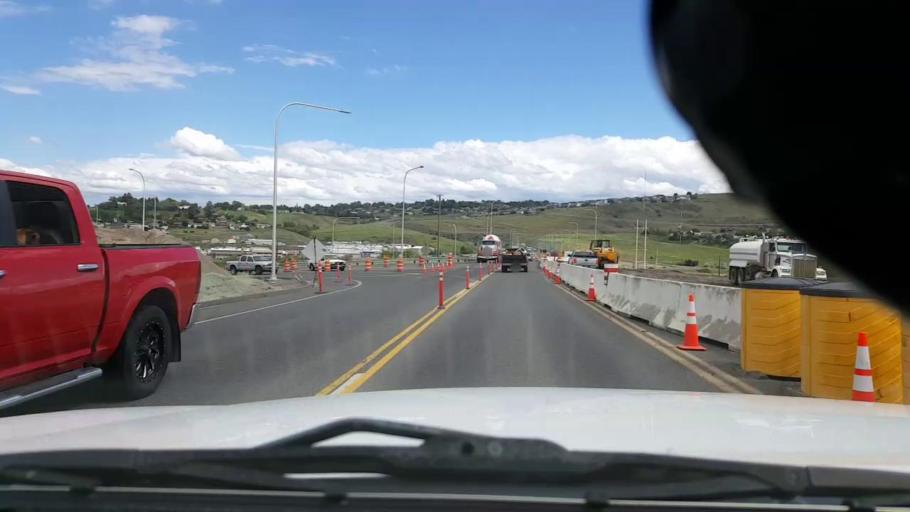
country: US
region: Washington
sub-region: Asotin County
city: West Clarkston-Highland
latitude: 46.3982
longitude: -117.0466
